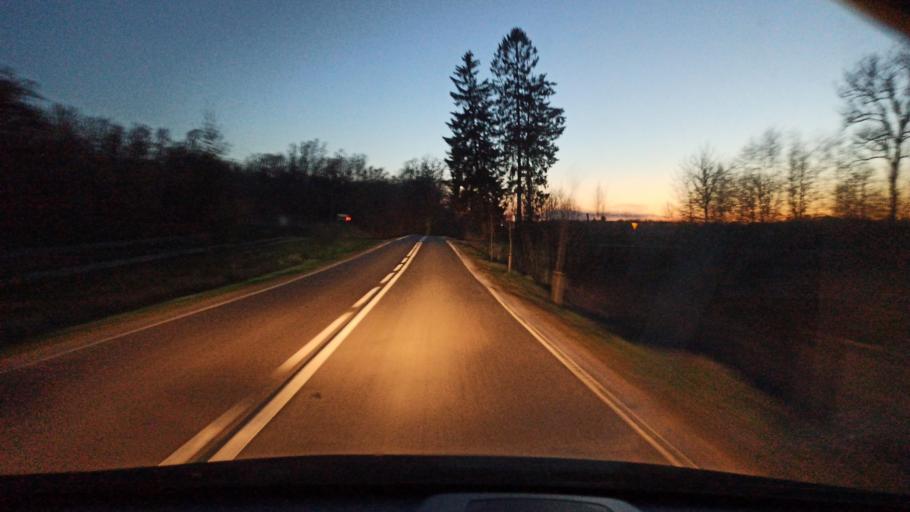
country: PL
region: Warmian-Masurian Voivodeship
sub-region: Powiat elblaski
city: Gronowo Gorne
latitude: 54.1686
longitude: 19.4906
